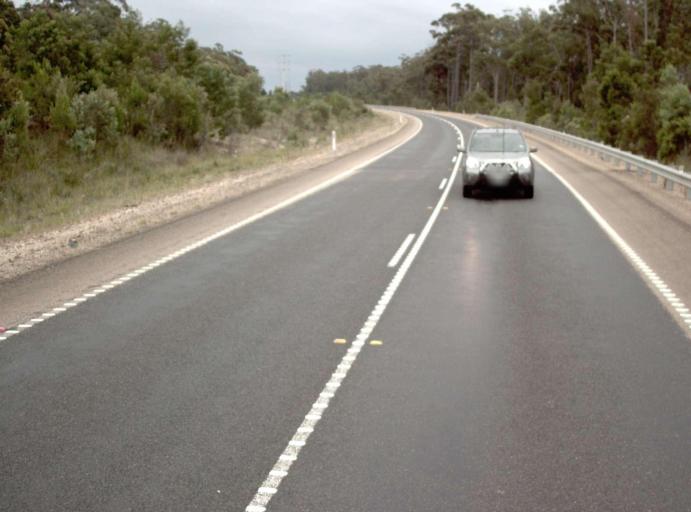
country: AU
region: Victoria
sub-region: East Gippsland
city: Lakes Entrance
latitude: -37.6977
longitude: 148.0487
